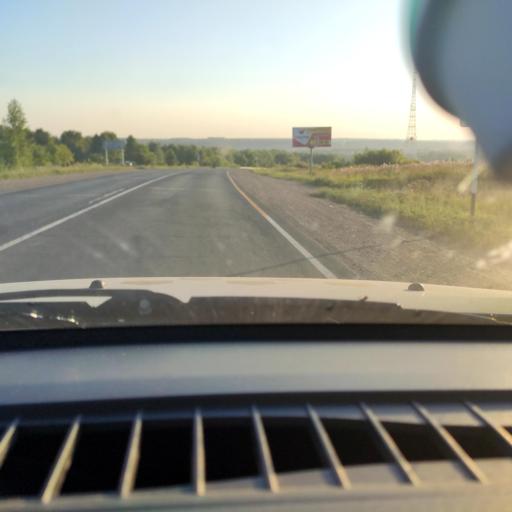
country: RU
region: Perm
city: Kungur
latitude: 57.4451
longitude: 56.9695
